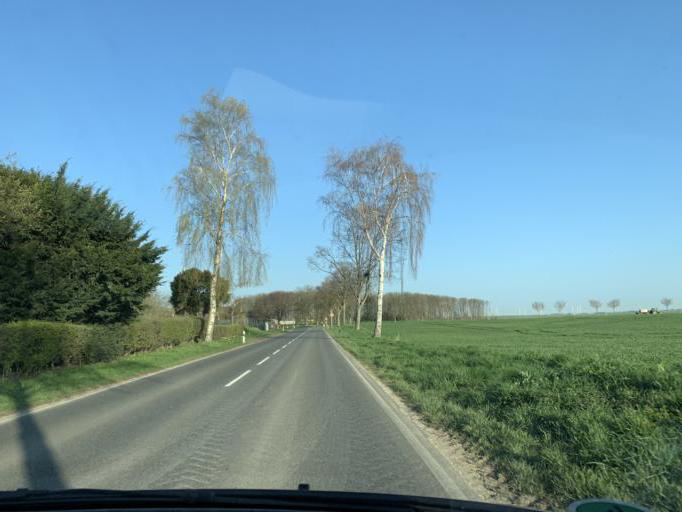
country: DE
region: North Rhine-Westphalia
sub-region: Regierungsbezirk Koln
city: Titz
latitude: 50.9667
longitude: 6.4633
